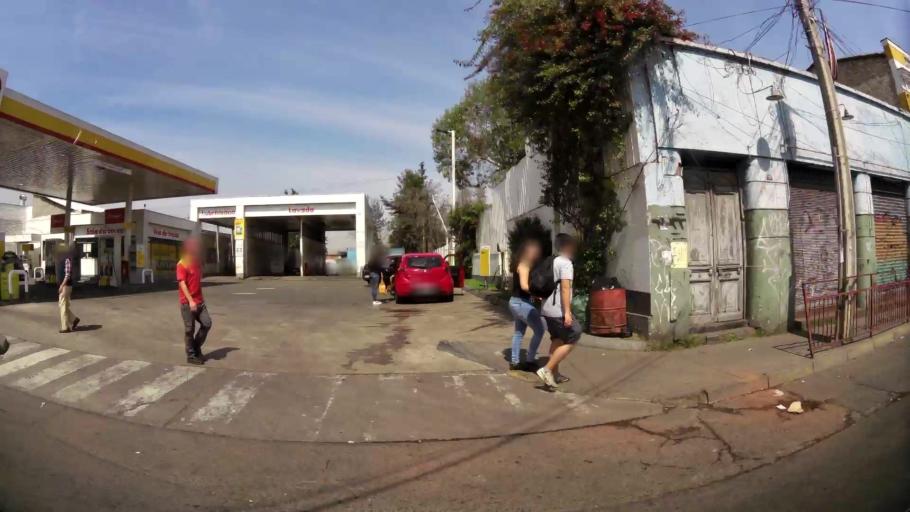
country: CL
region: Santiago Metropolitan
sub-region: Provincia de Santiago
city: Lo Prado
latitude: -33.4235
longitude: -70.6905
